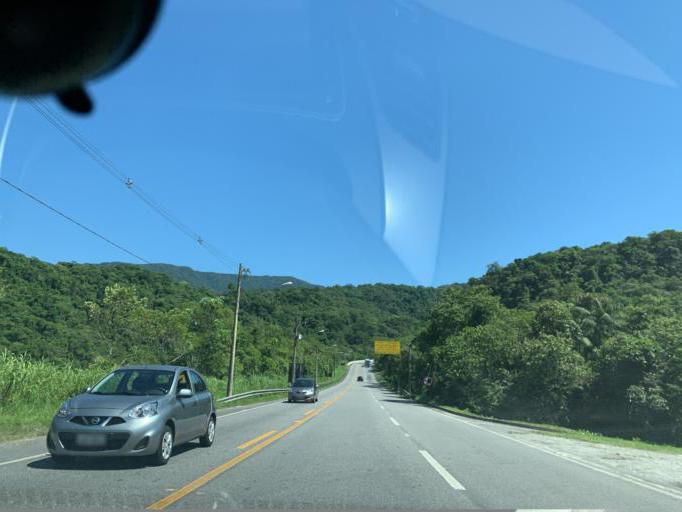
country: BR
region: Sao Paulo
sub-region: Bertioga
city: Bertioga
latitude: -23.7577
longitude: -46.0390
